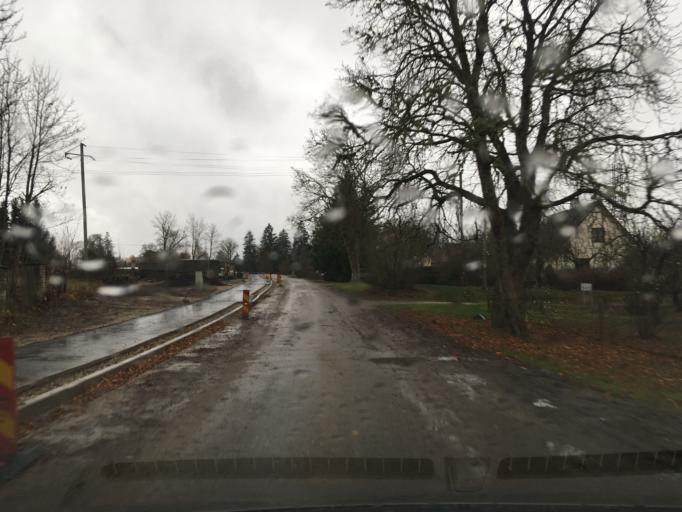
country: EE
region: Laeaene
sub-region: Lihula vald
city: Lihula
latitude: 58.6816
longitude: 23.8233
